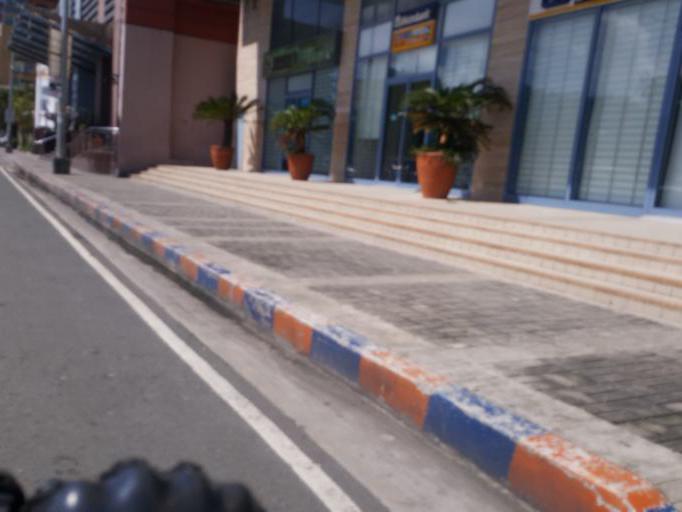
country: PH
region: Metro Manila
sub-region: City of Manila
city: Port Area
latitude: 14.5764
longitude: 120.9796
